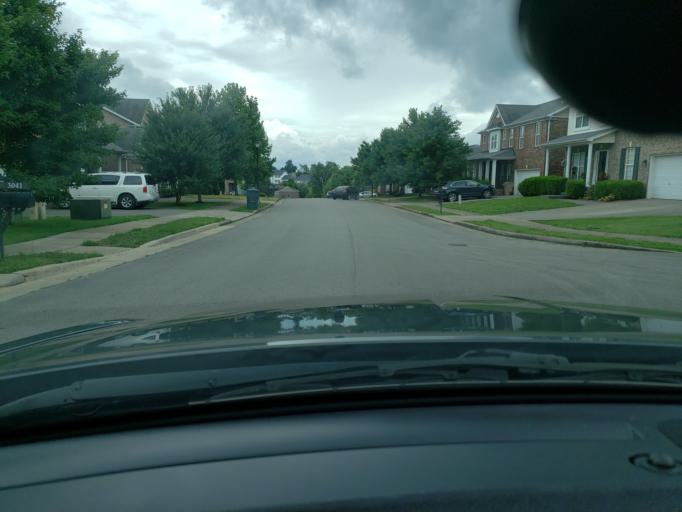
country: US
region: Tennessee
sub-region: Williamson County
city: Nolensville
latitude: 36.0250
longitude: -86.6968
